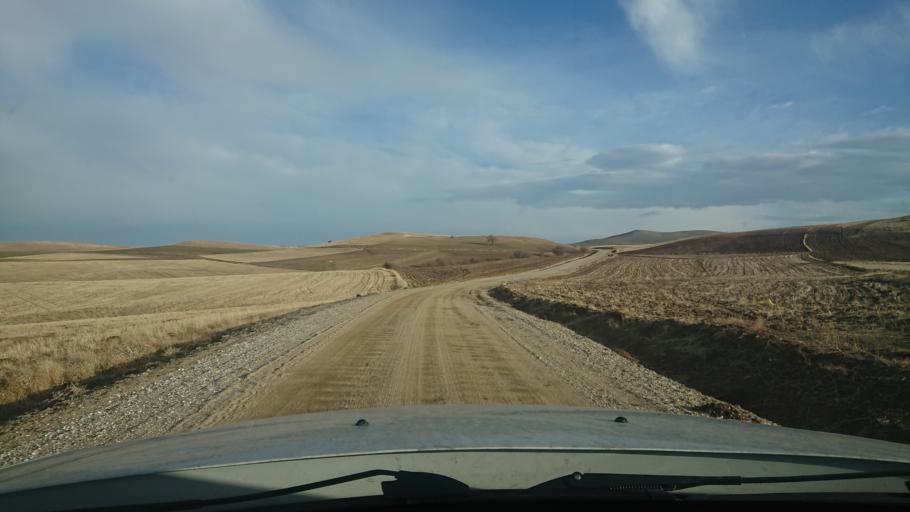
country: TR
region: Aksaray
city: Acipinar
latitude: 38.6932
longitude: 33.8701
